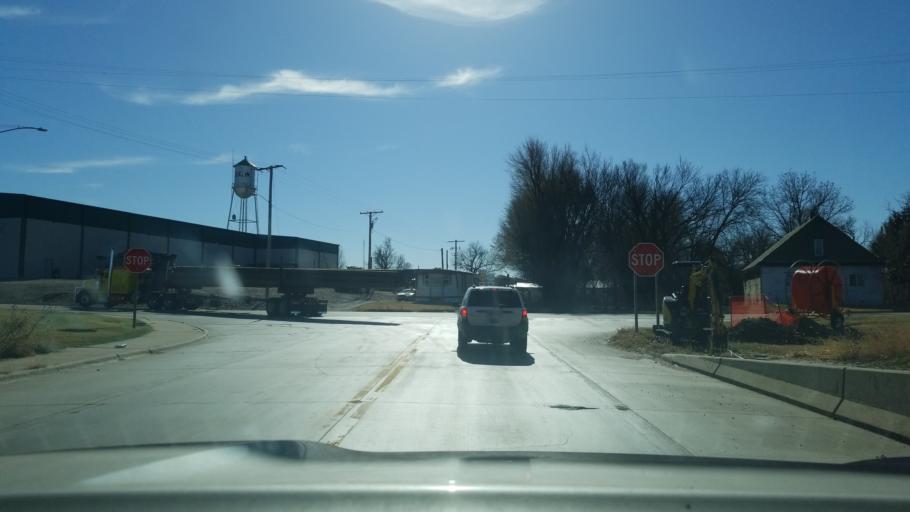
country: US
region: Kansas
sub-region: Kiowa County
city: Greensburg
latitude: 37.5518
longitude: -99.6364
